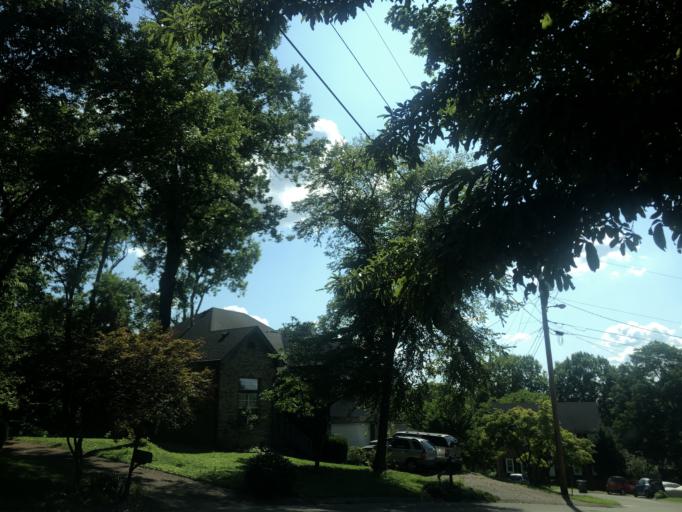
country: US
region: Tennessee
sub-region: Wilson County
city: Green Hill
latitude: 36.1908
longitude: -86.5993
